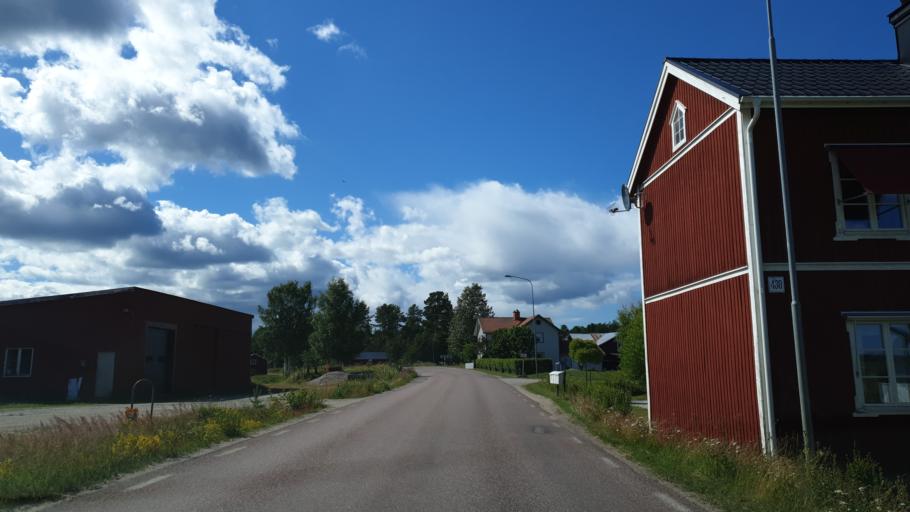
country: SE
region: Gaevleborg
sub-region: Nordanstigs Kommun
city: Bergsjoe
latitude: 62.0524
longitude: 17.1991
